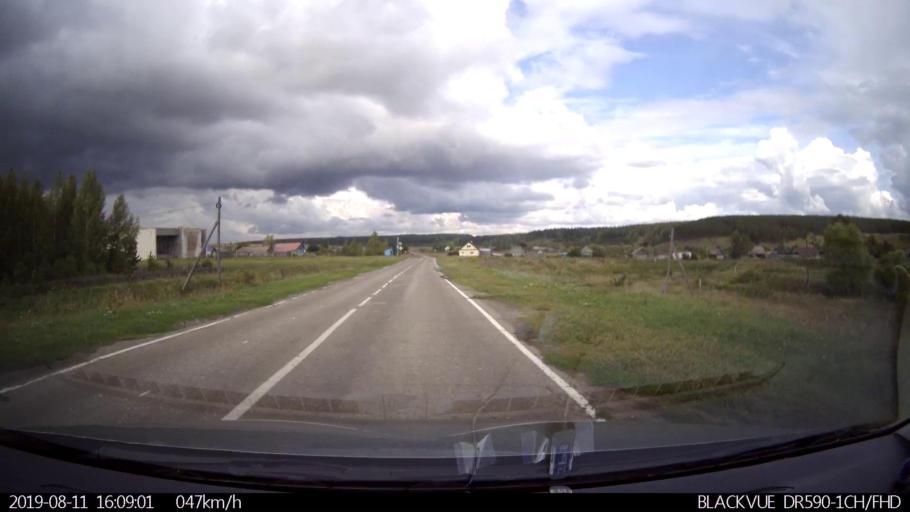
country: RU
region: Ulyanovsk
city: Ignatovka
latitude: 53.9892
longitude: 47.6508
